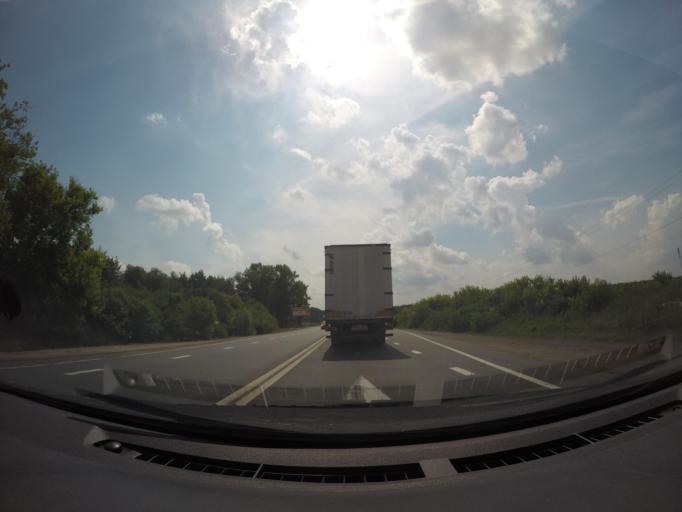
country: RU
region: Moskovskaya
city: Malyshevo
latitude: 55.4867
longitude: 38.3431
